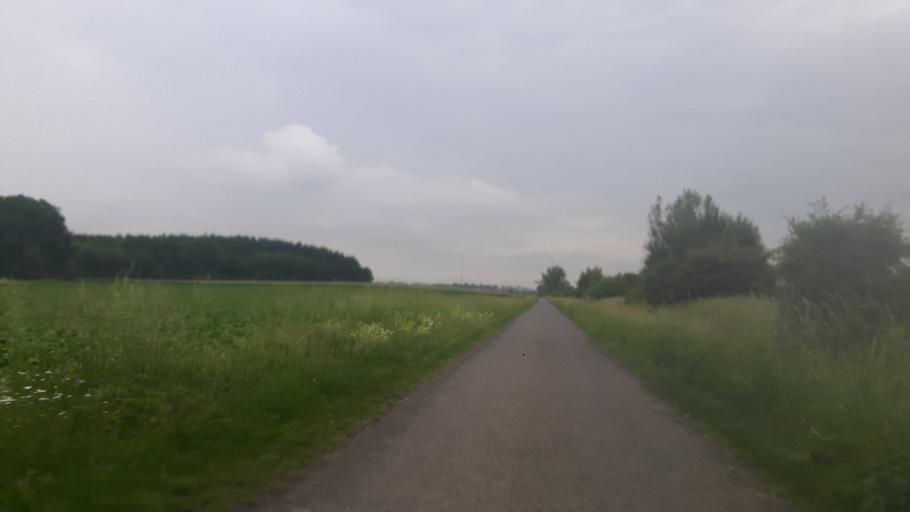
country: DE
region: Bavaria
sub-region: Regierungsbezirk Unterfranken
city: Oberpleichfeld
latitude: 49.8920
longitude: 10.1068
